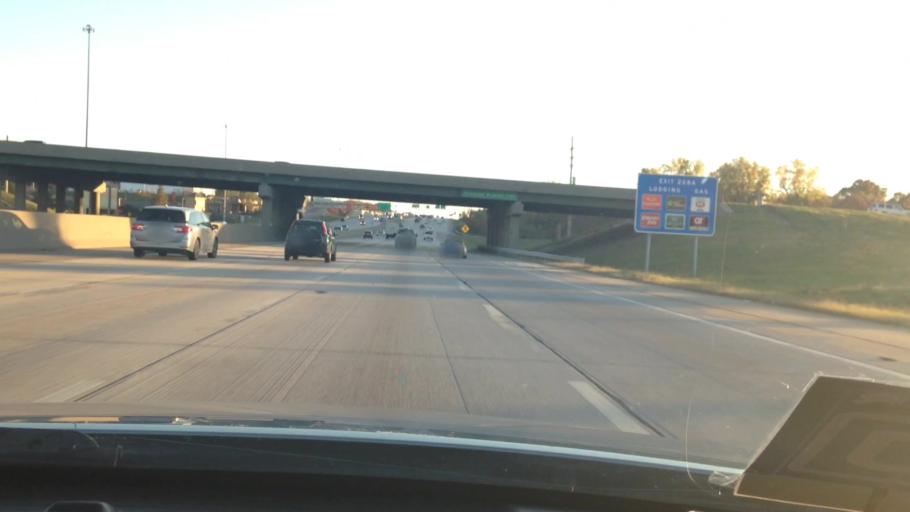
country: US
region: Kansas
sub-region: Johnson County
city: Merriam
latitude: 39.0157
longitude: -94.6933
